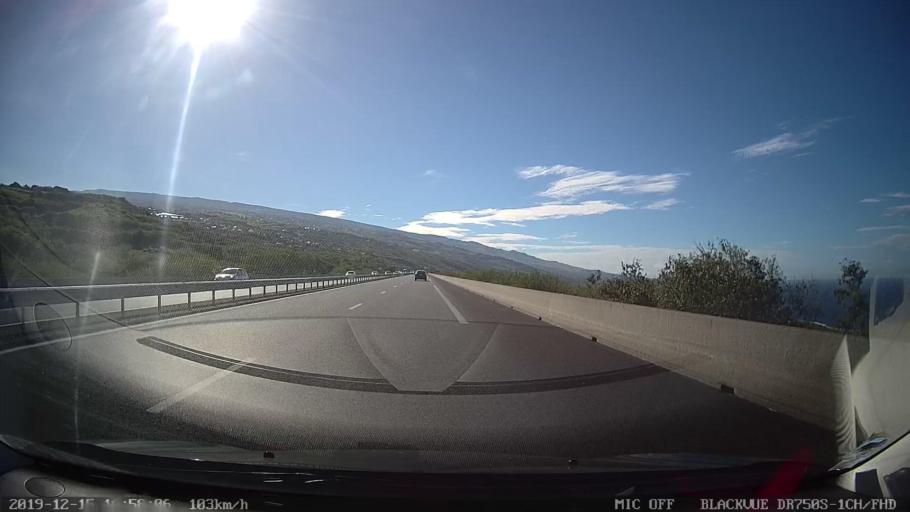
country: RE
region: Reunion
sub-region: Reunion
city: Trois-Bassins
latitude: -21.0950
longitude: 55.2606
